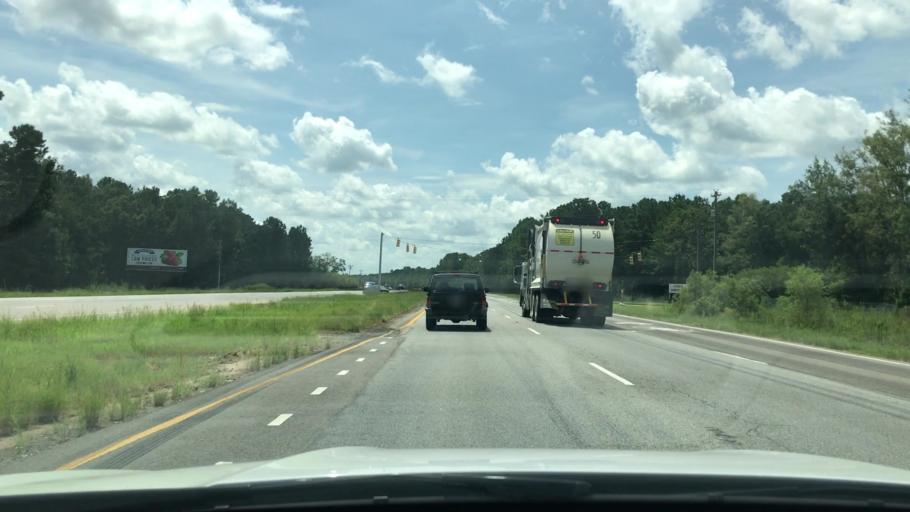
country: US
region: South Carolina
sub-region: Berkeley County
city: Goose Creek
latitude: 33.0650
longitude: -80.0349
